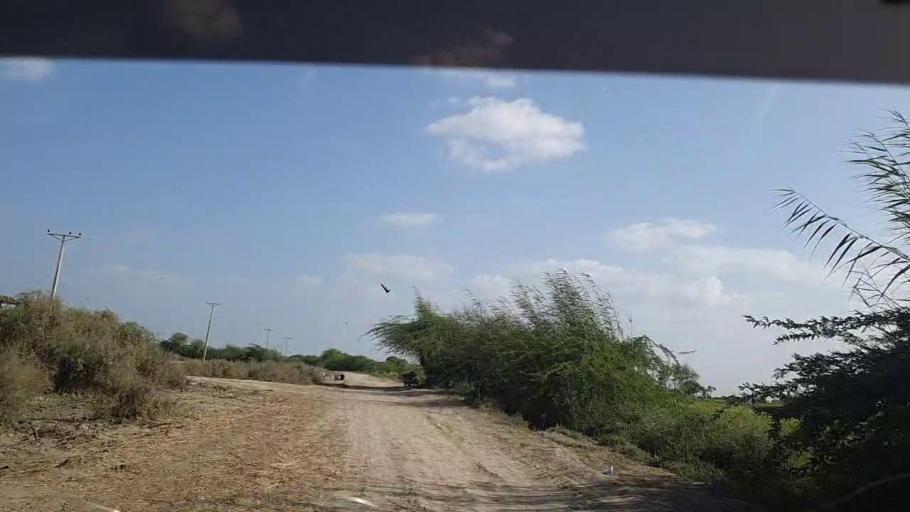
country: PK
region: Sindh
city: Kadhan
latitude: 24.4621
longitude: 68.8531
